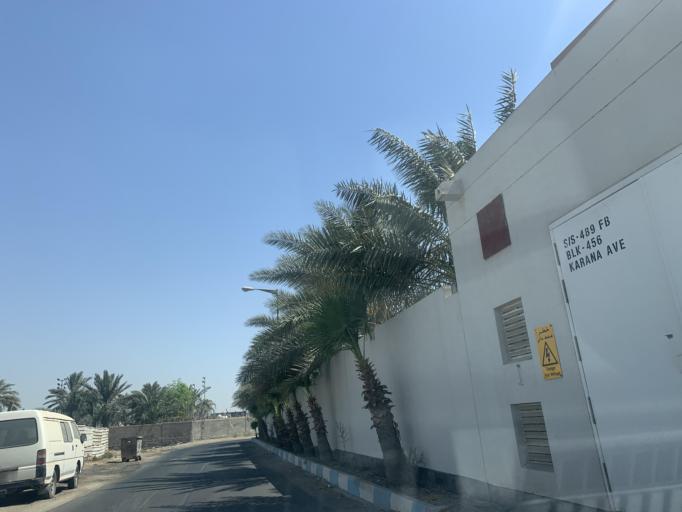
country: BH
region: Manama
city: Jidd Hafs
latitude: 26.2239
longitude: 50.5073
